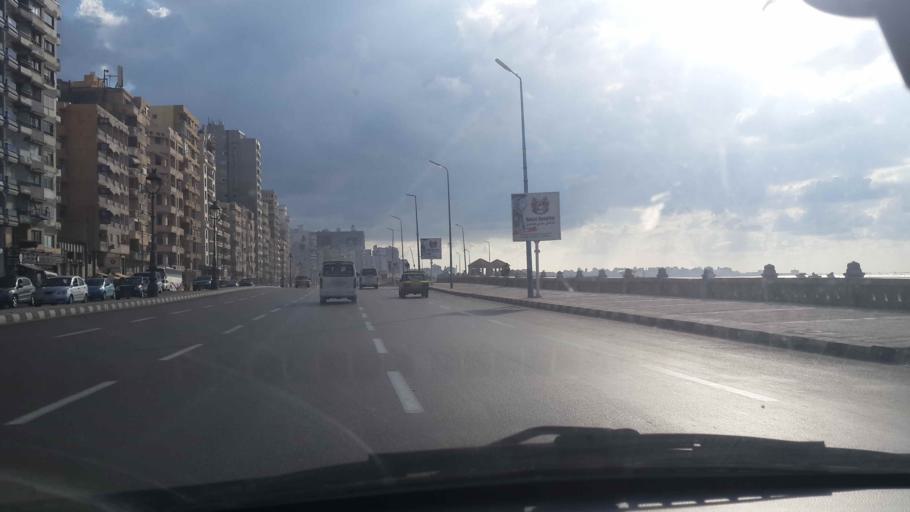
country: EG
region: Alexandria
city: Alexandria
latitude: 31.2210
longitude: 29.9307
